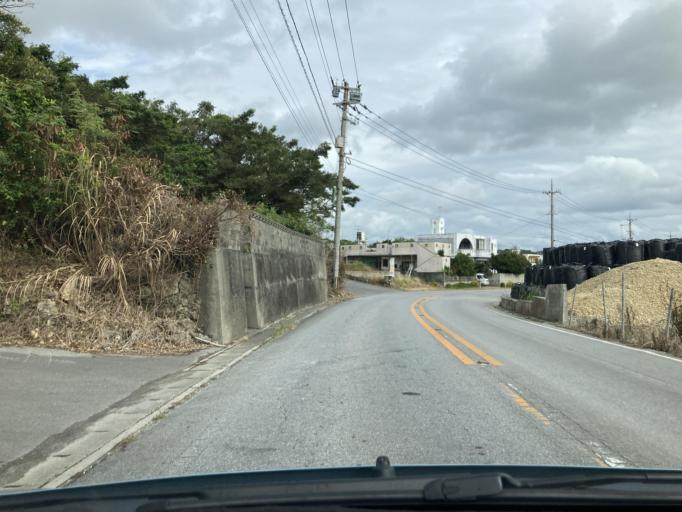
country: JP
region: Okinawa
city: Itoman
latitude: 26.1218
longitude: 127.6787
